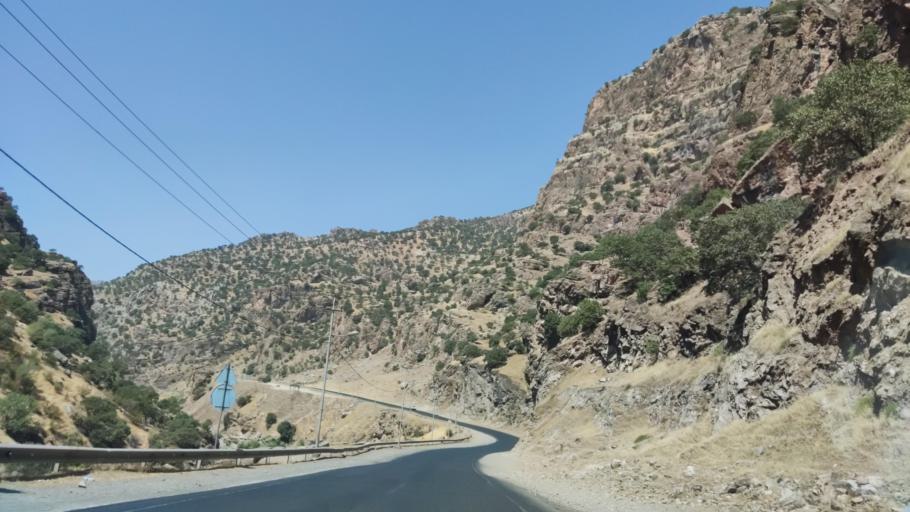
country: IQ
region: Arbil
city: Ruwandiz
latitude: 36.6308
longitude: 44.4820
